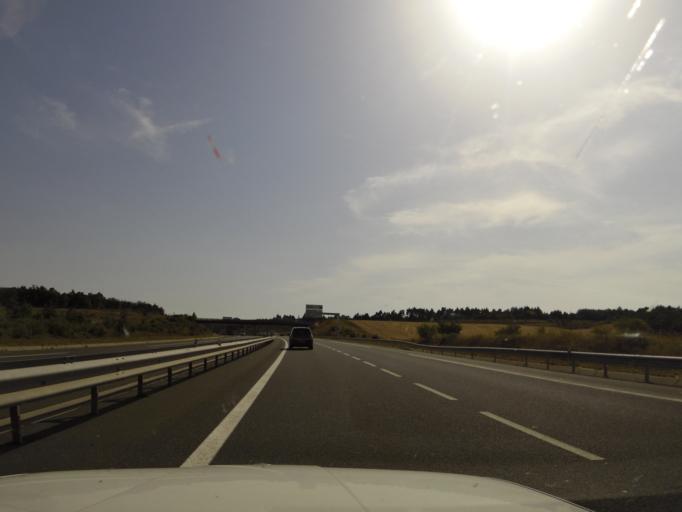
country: FR
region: Midi-Pyrenees
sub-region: Departement de l'Aveyron
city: Millau
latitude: 44.1805
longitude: 3.0382
